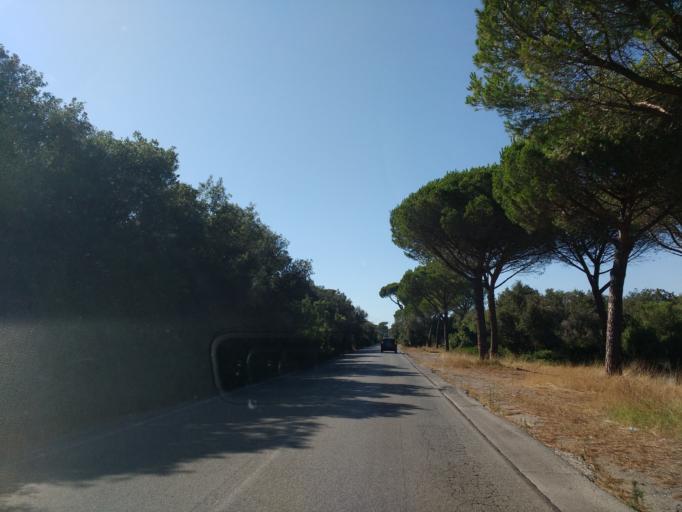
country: IT
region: Latium
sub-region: Citta metropolitana di Roma Capitale
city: Acilia-Castel Fusano-Ostia Antica
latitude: 41.7160
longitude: 12.3535
